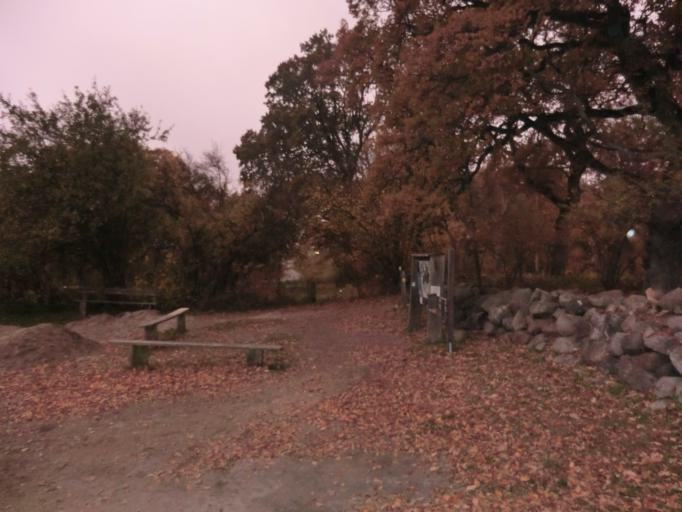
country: SE
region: Skane
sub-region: Lunds Kommun
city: Genarp
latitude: 55.6723
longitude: 13.3301
